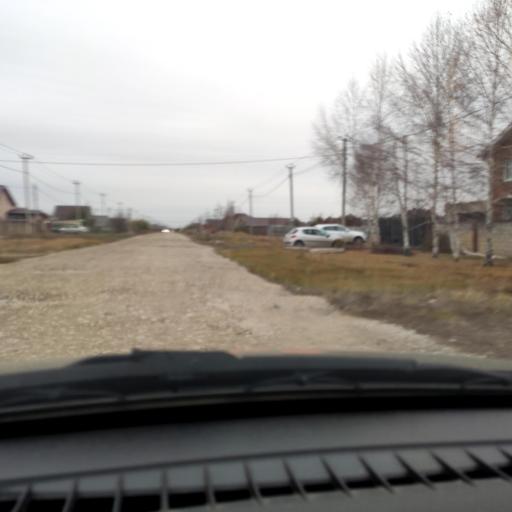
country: RU
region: Samara
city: Podstepki
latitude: 53.5239
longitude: 49.1541
